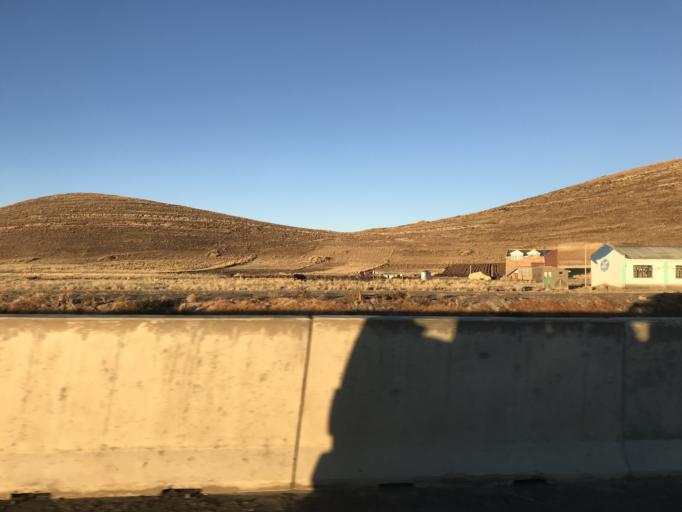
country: BO
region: La Paz
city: Batallas
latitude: -16.3032
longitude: -68.4821
